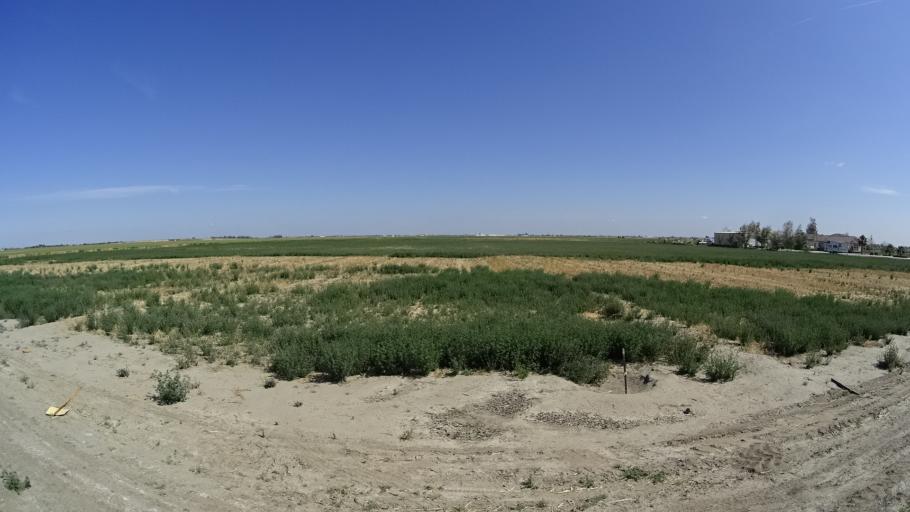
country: US
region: California
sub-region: Kings County
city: Lemoore
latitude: 36.2550
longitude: -119.8199
